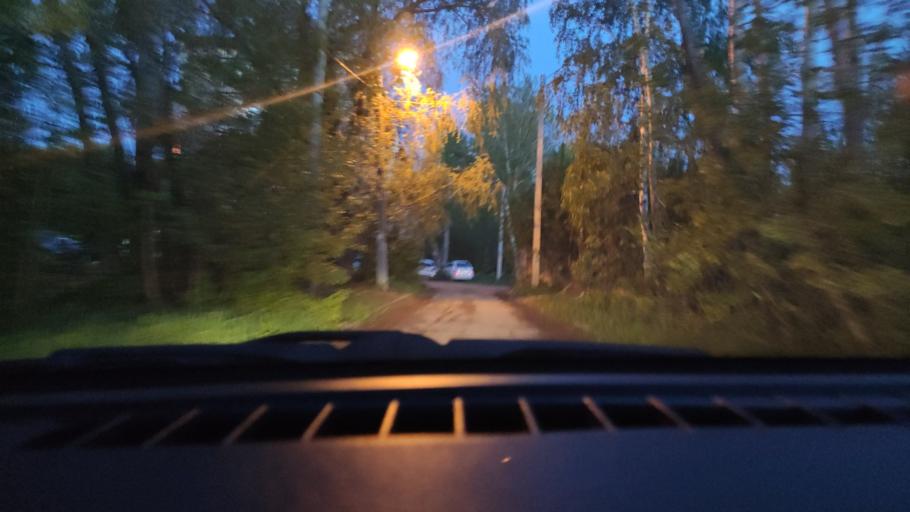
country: RU
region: Perm
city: Perm
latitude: 58.1048
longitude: 56.3820
